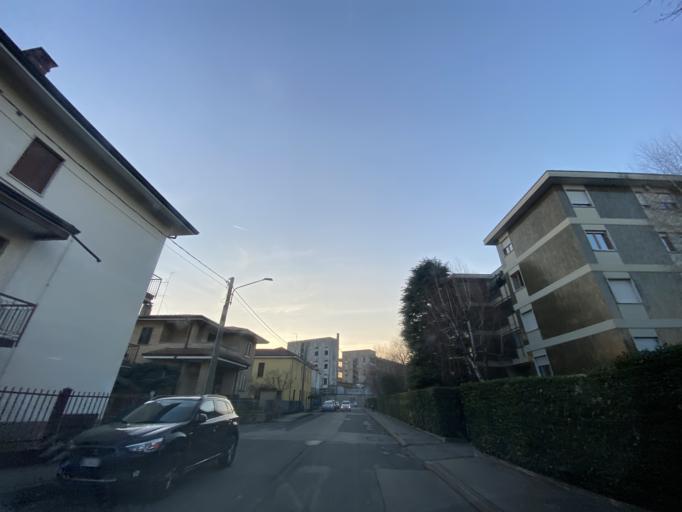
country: IT
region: Lombardy
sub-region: Provincia di Varese
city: Saronno
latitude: 45.6311
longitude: 9.0478
